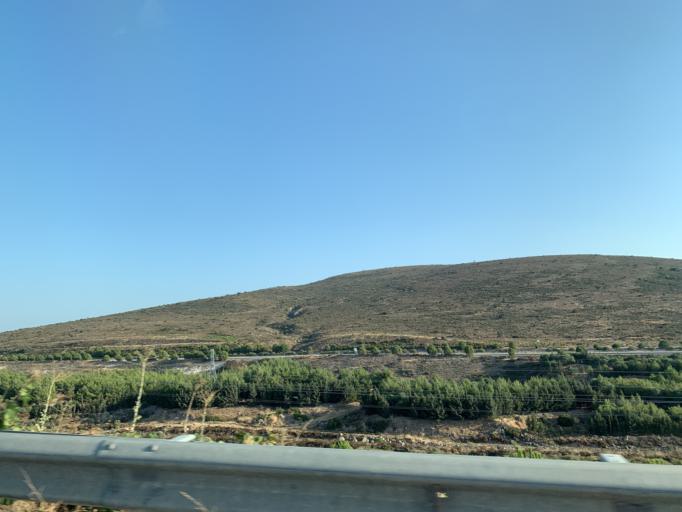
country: TR
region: Izmir
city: Alacati
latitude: 38.2763
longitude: 26.4098
